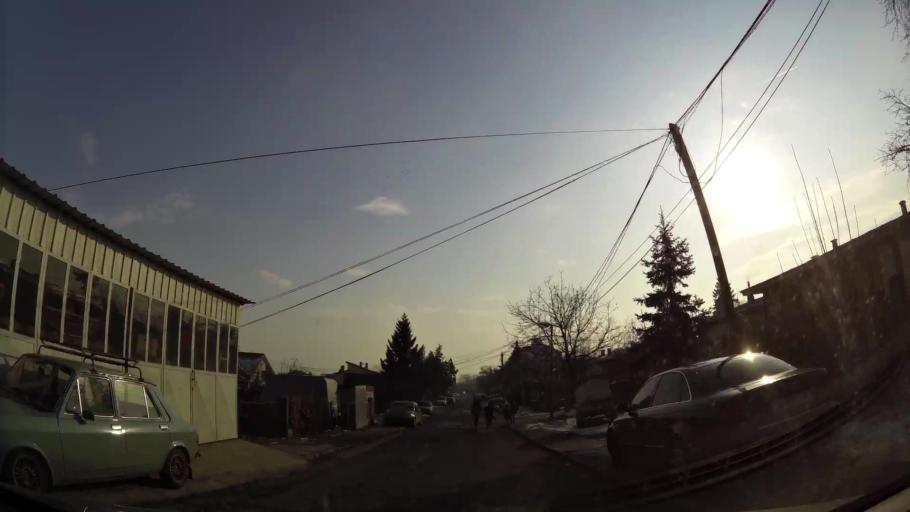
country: MK
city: Creshevo
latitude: 42.0155
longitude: 21.5084
